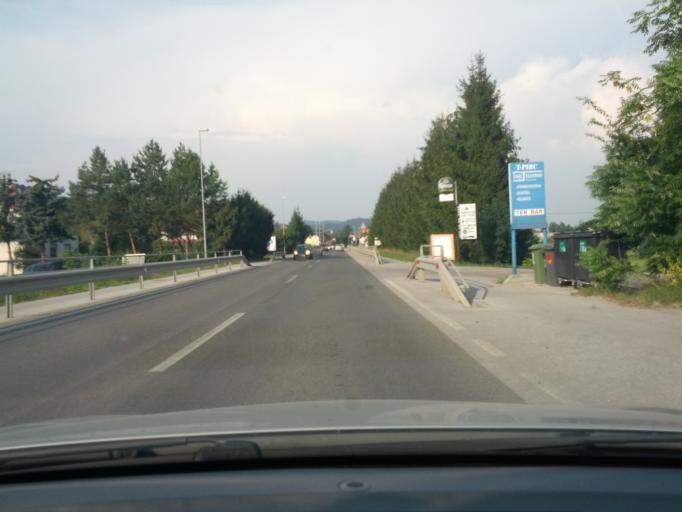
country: SI
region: Vrhnika
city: Verd
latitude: 45.9920
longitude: 14.3253
